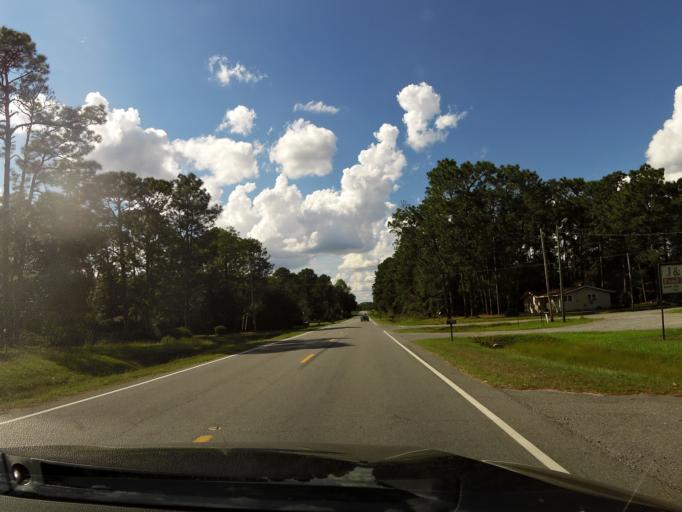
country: US
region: Georgia
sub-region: Lowndes County
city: Valdosta
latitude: 30.7999
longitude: -83.1961
